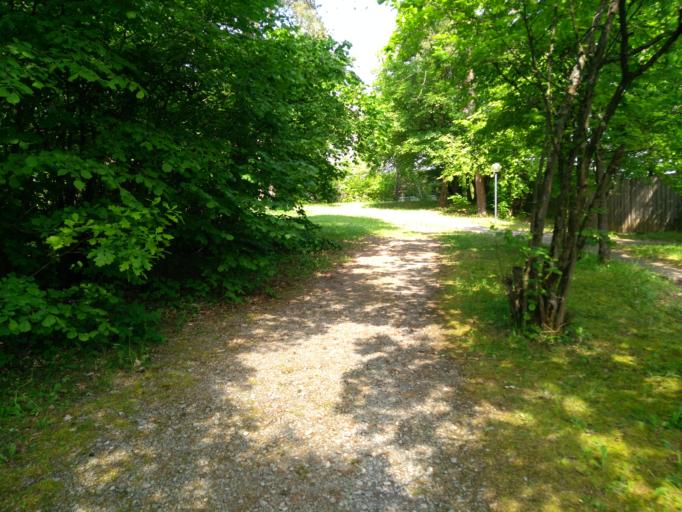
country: DE
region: Bavaria
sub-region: Regierungsbezirk Unterfranken
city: Bad Kissingen
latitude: 50.1896
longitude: 10.0900
